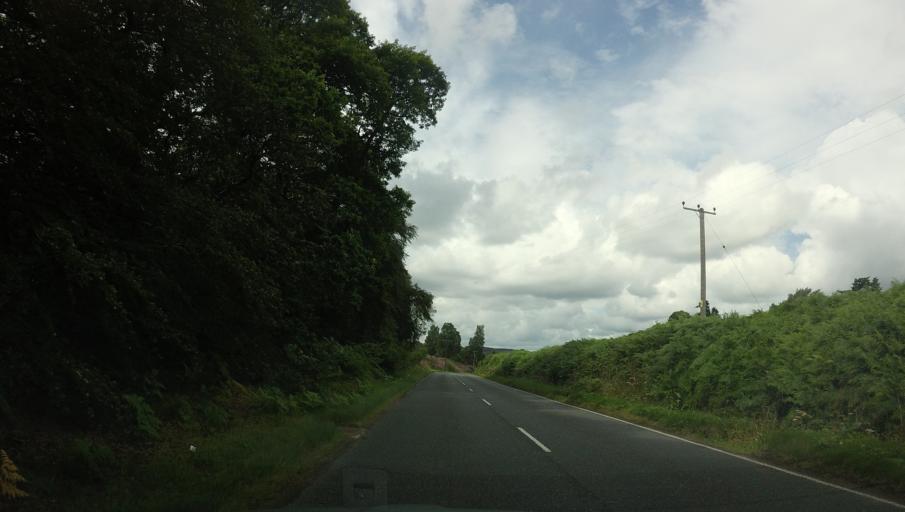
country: GB
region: Scotland
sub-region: Aberdeenshire
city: Banchory
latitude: 57.0583
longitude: -2.5459
